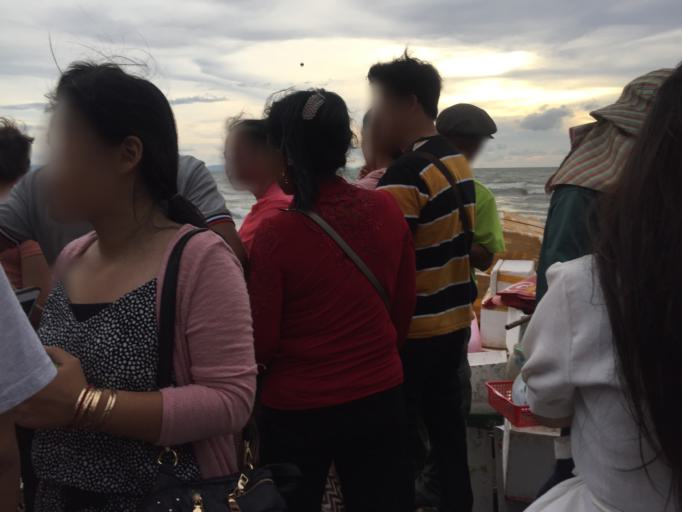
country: KH
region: Kep
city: Krong Kep
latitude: 10.4888
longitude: 104.2888
